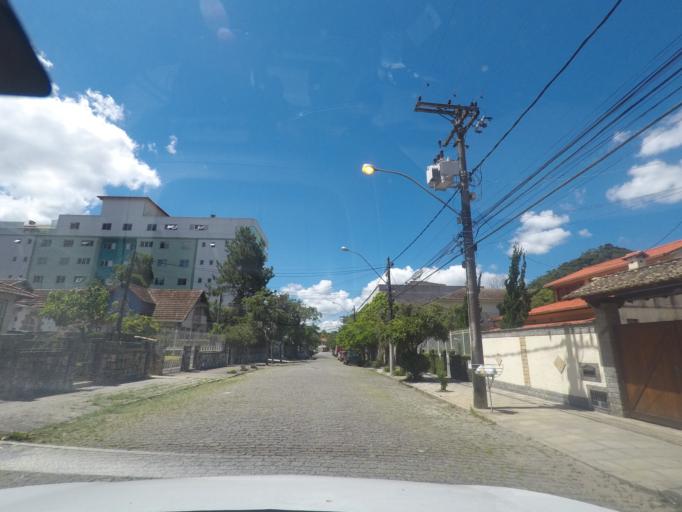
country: BR
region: Rio de Janeiro
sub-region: Teresopolis
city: Teresopolis
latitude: -22.4346
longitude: -42.9774
